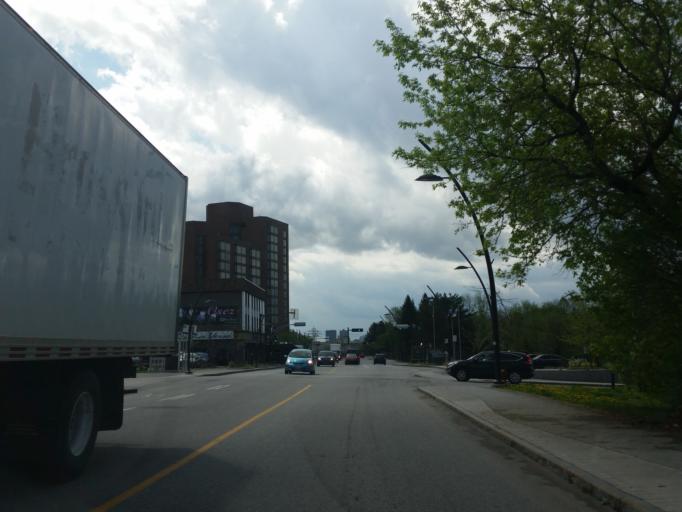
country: CA
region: Ontario
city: Ottawa
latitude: 45.4269
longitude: -75.7244
